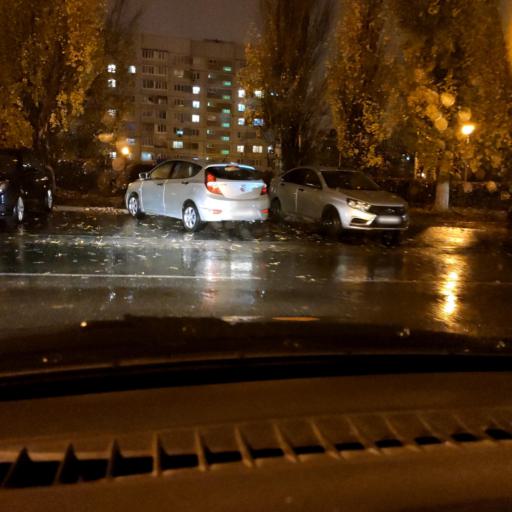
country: RU
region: Samara
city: Tol'yatti
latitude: 53.5372
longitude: 49.3358
